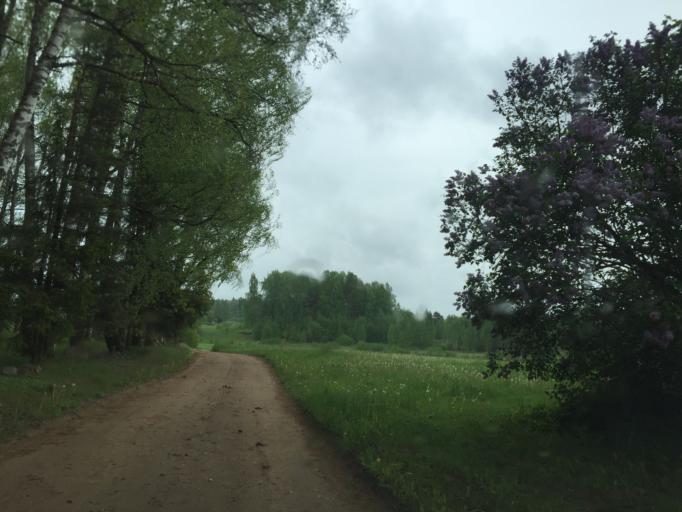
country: LV
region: Kegums
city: Kegums
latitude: 56.7356
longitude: 24.7429
